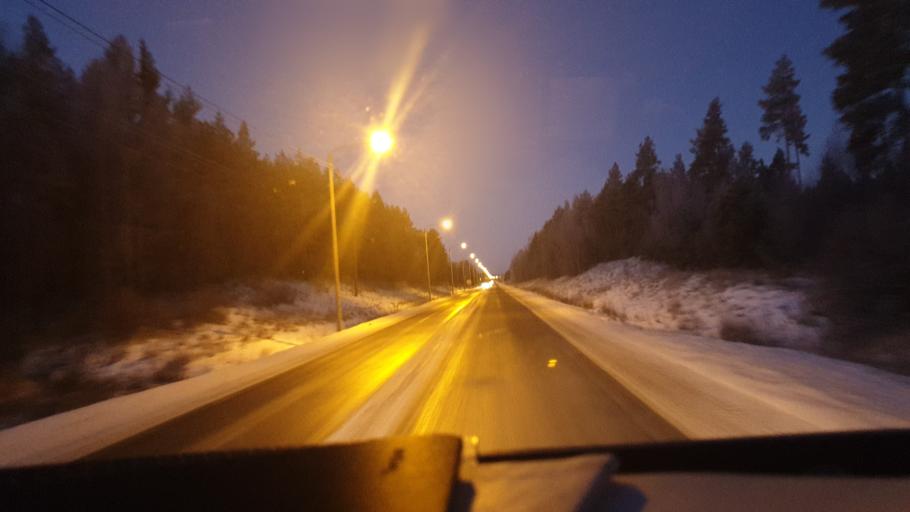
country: FI
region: Northern Ostrobothnia
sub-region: Raahe
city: Raahe
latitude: 64.6904
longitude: 24.6316
